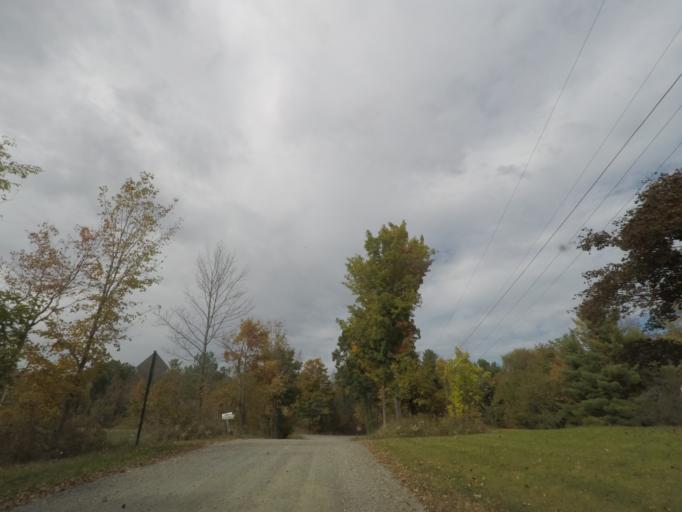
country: US
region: New York
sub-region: Rensselaer County
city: West Sand Lake
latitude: 42.5860
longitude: -73.6130
